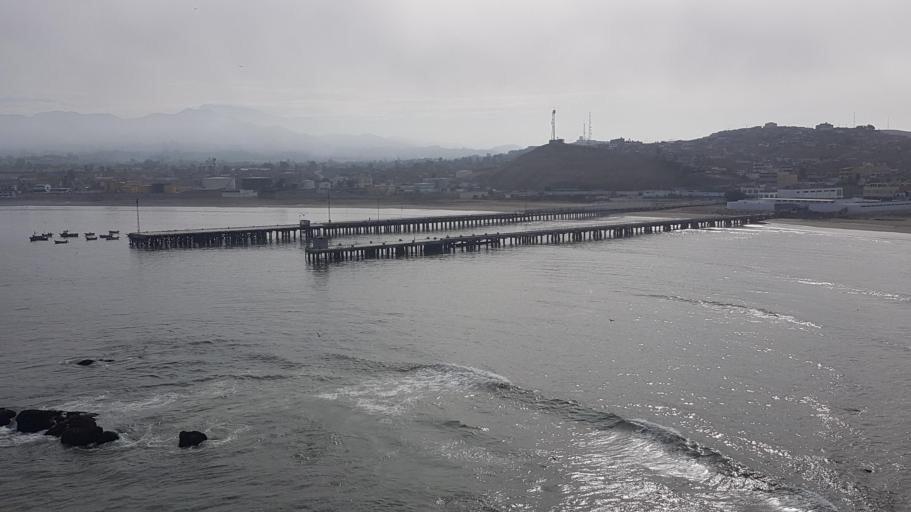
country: PE
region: Lima
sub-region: Barranca
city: Puerto Supe
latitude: -10.7997
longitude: -77.7508
